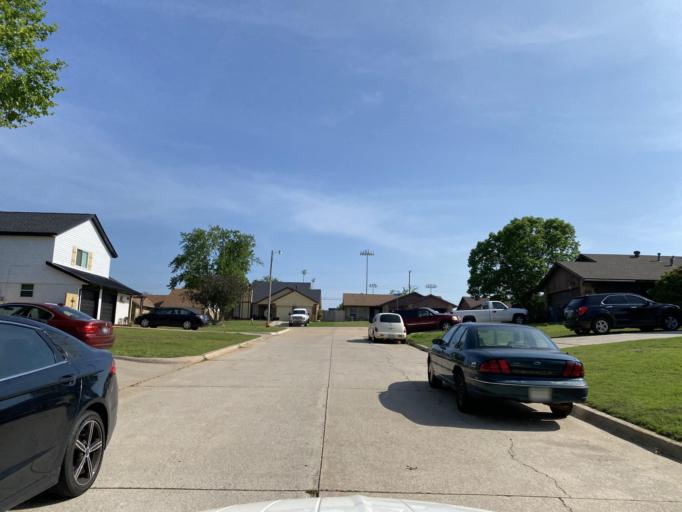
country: US
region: Oklahoma
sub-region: Oklahoma County
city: Midwest City
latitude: 35.4470
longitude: -97.3553
